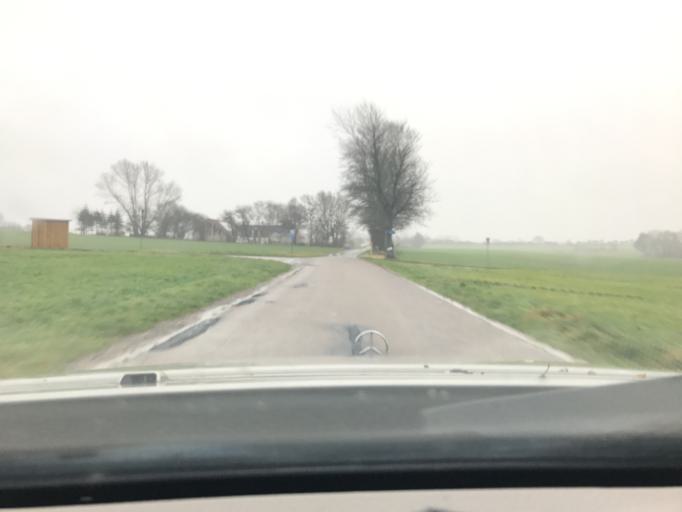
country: DK
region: South Denmark
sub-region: Sonderborg Kommune
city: Horuphav
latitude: 54.8908
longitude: 10.0428
